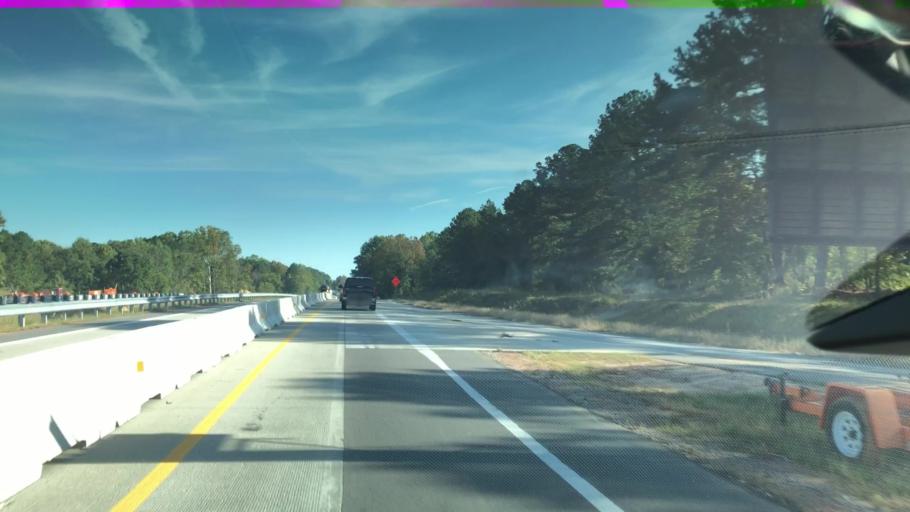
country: US
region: North Carolina
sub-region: Vance County
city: Henderson
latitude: 36.3488
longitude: -78.3922
